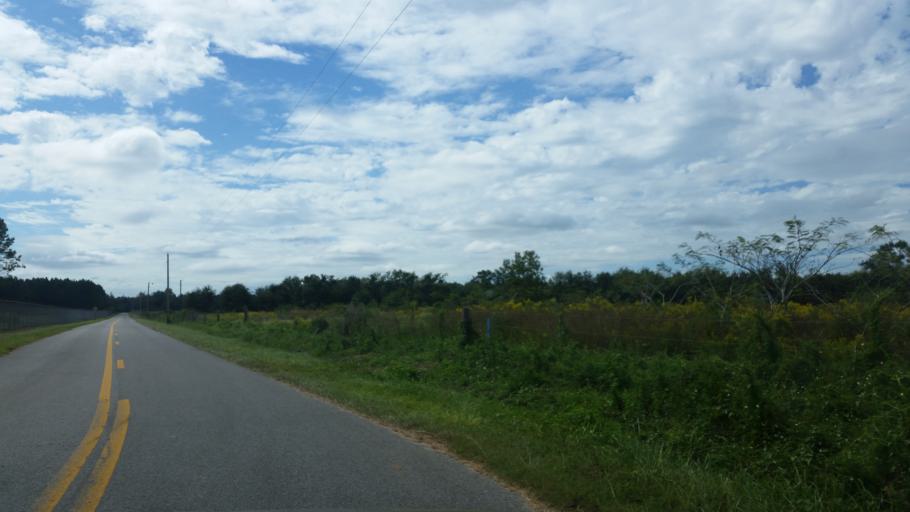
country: US
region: Florida
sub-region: Santa Rosa County
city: Point Baker
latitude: 30.7381
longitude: -87.0326
